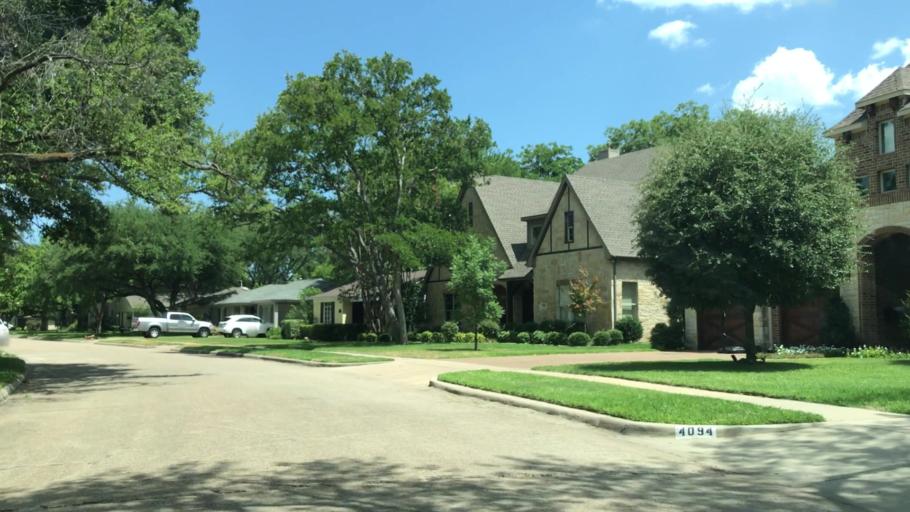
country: US
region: Texas
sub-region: Dallas County
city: University Park
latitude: 32.8728
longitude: -96.8436
